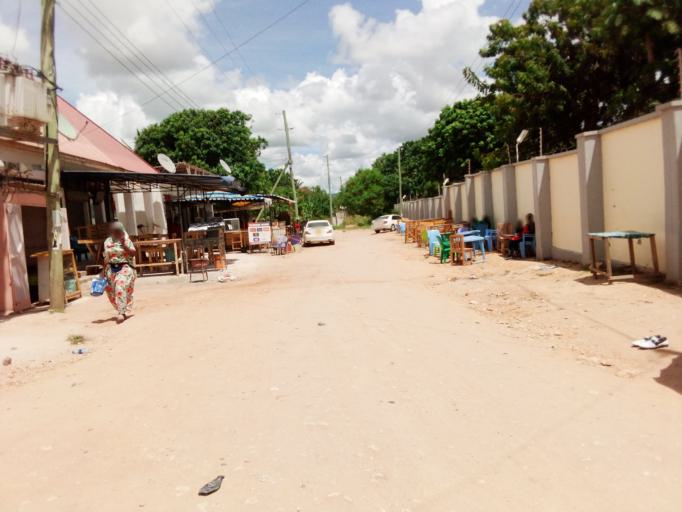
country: TZ
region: Dodoma
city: Dodoma
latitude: -6.1615
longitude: 35.7637
